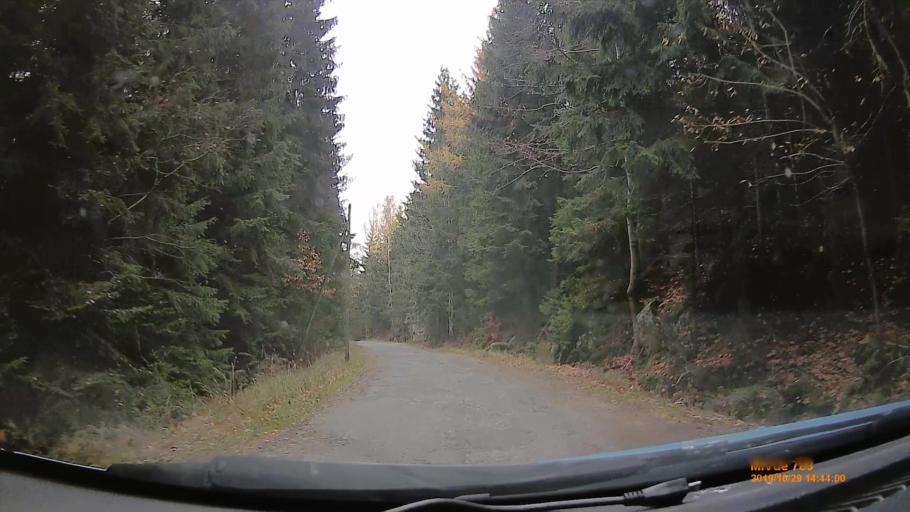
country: PL
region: Lower Silesian Voivodeship
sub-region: Powiat klodzki
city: Szczytna
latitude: 50.4459
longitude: 16.4206
